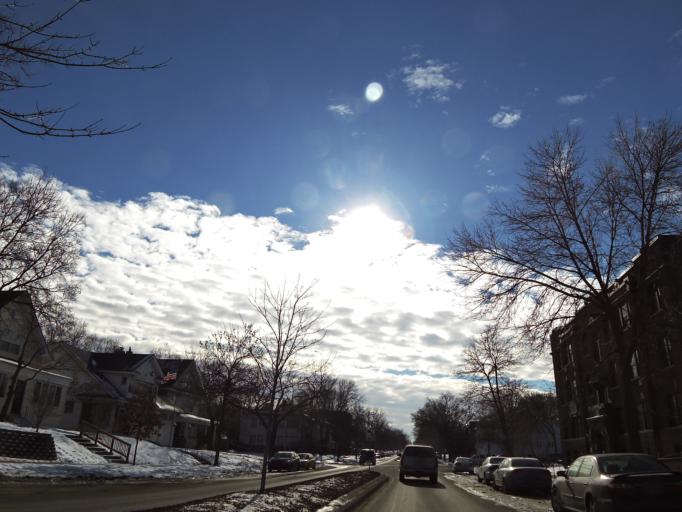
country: US
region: Minnesota
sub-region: Hennepin County
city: Minneapolis
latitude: 44.9455
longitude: -93.2882
